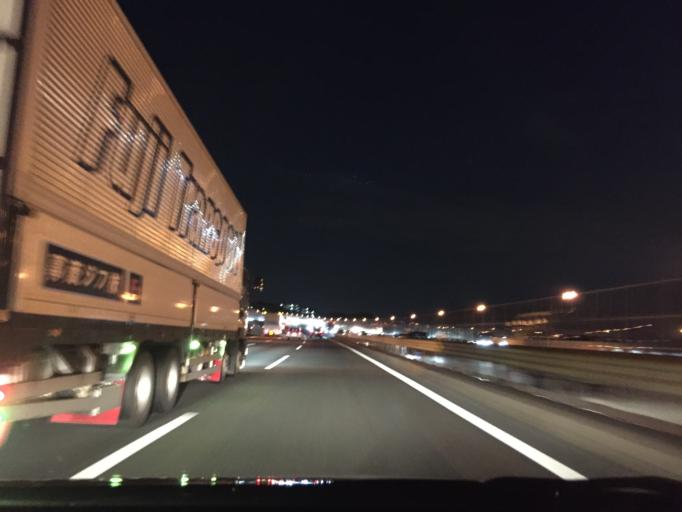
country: JP
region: Tokyo
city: Chofugaoka
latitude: 35.6123
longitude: 139.5890
